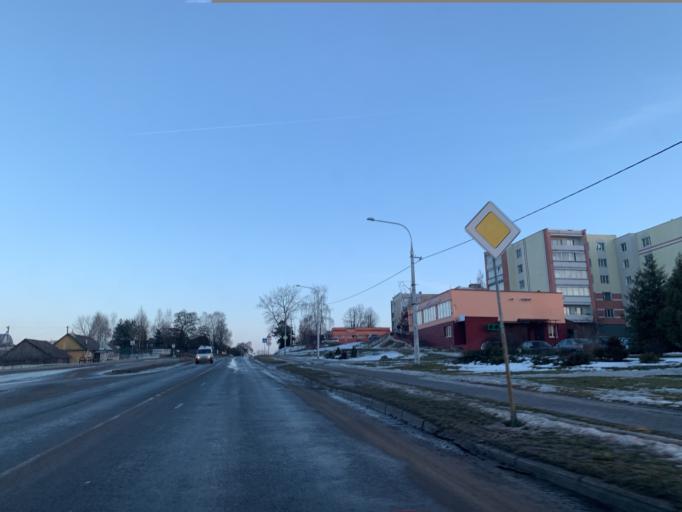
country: BY
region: Minsk
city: Nyasvizh
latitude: 53.2333
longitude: 26.6508
